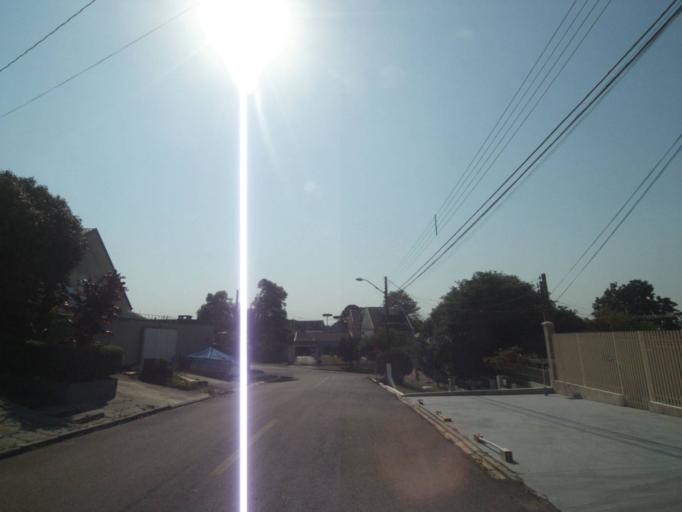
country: BR
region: Parana
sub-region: Sao Jose Dos Pinhais
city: Sao Jose dos Pinhais
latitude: -25.4955
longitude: -49.2627
